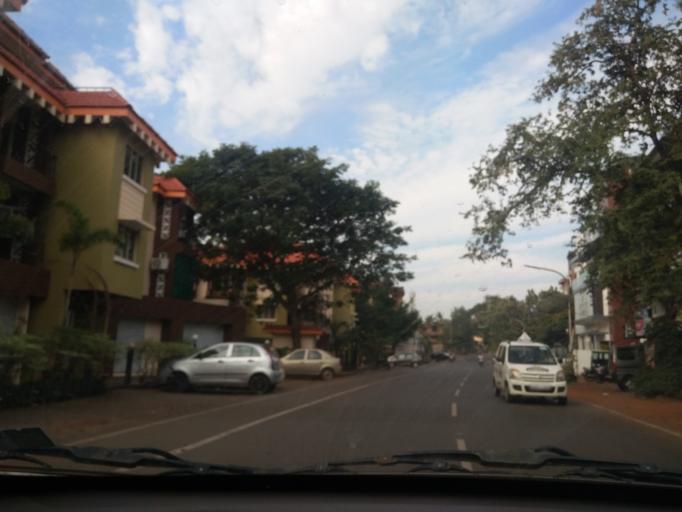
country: IN
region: Goa
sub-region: South Goa
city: Raia
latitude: 15.2899
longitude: 73.9705
